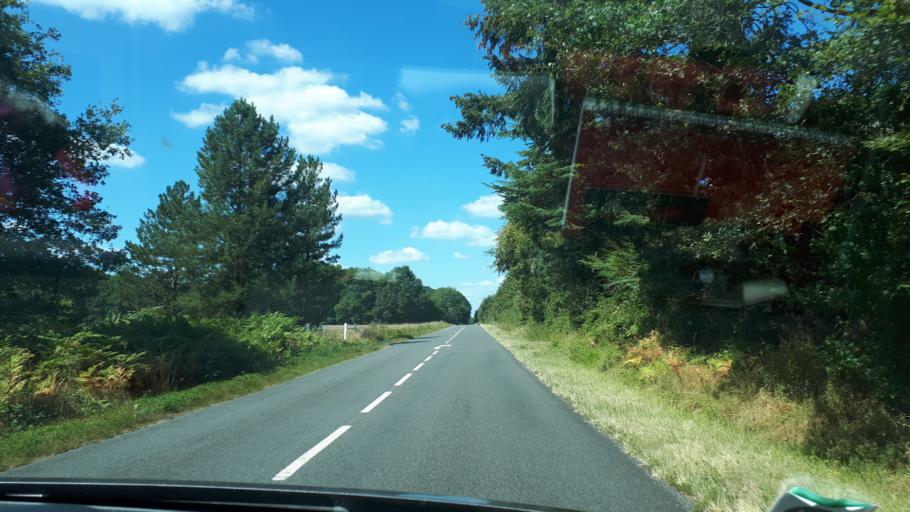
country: FR
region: Centre
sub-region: Departement du Loir-et-Cher
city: Neung-sur-Beuvron
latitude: 47.5348
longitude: 1.7806
